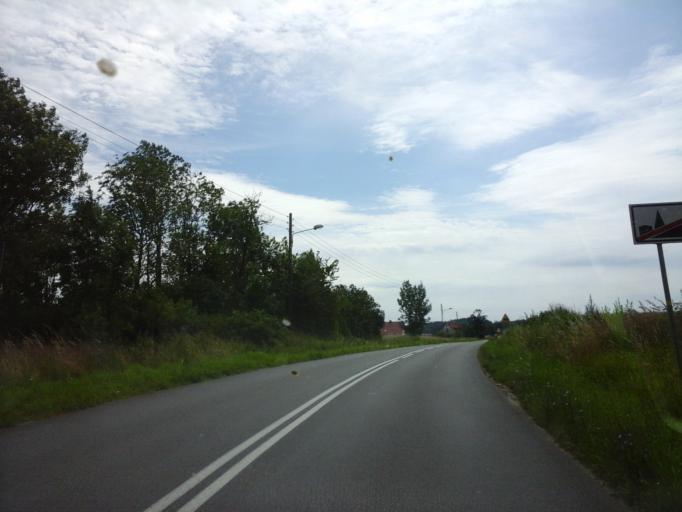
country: PL
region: Lubusz
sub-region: Powiat strzelecko-drezdenecki
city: Dobiegniew
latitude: 53.0104
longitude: 15.7371
